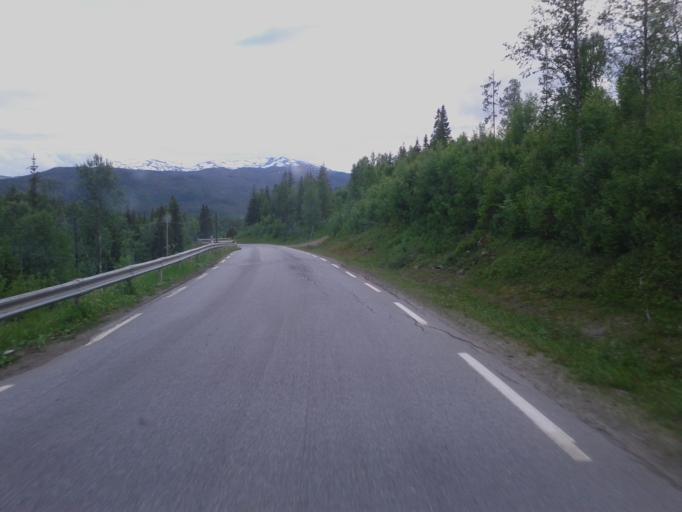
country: NO
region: Nordland
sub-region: Grane
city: Trofors
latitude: 65.5390
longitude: 13.6908
